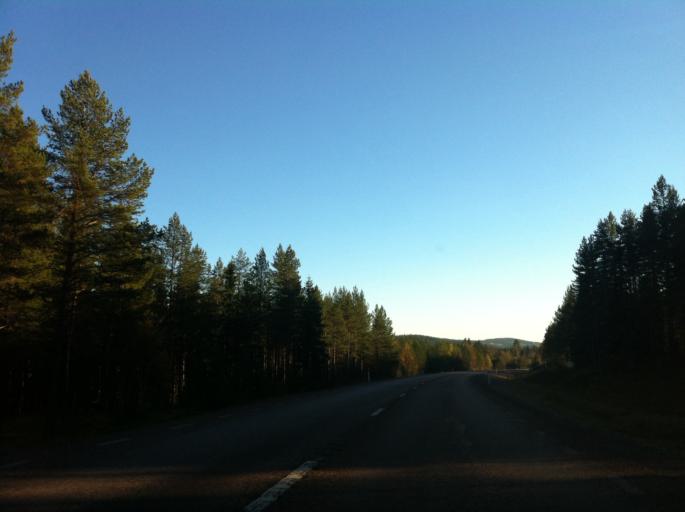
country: SE
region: Dalarna
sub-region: Rattviks Kommun
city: Raettvik
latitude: 60.8241
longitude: 15.2512
